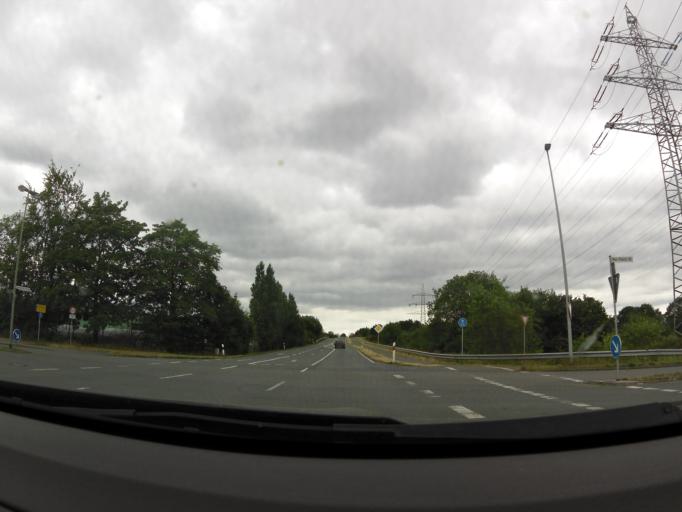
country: DE
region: North Rhine-Westphalia
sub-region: Regierungsbezirk Dusseldorf
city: Voerde
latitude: 51.6319
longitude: 6.6864
